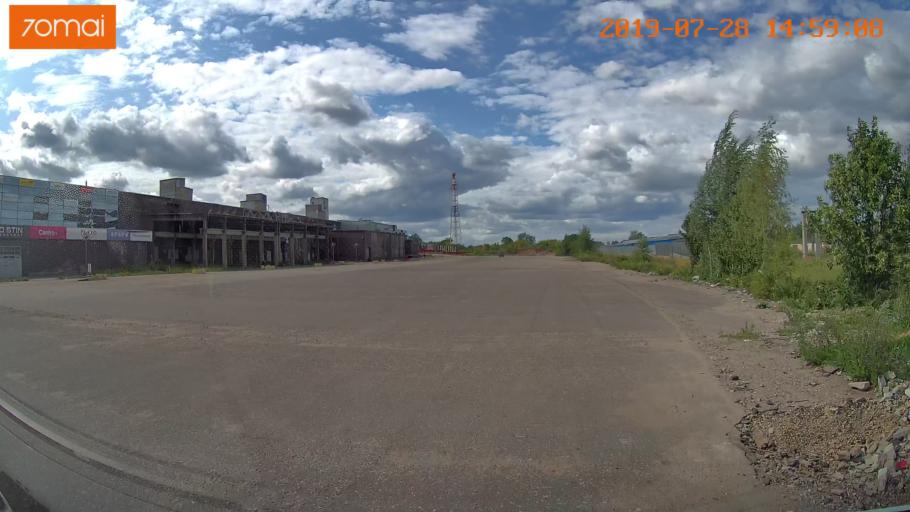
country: RU
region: Ivanovo
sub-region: Gorod Ivanovo
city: Ivanovo
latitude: 56.9675
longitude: 41.0269
